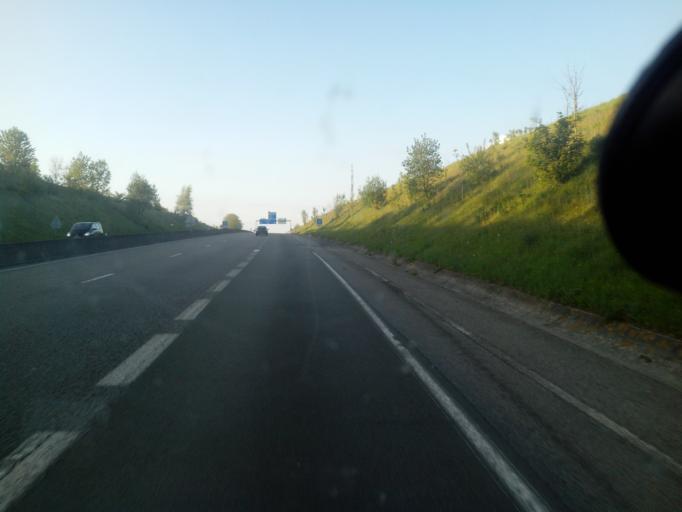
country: FR
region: Haute-Normandie
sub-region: Departement de la Seine-Maritime
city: Neufchatel-en-Bray
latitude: 49.7371
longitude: 1.4698
